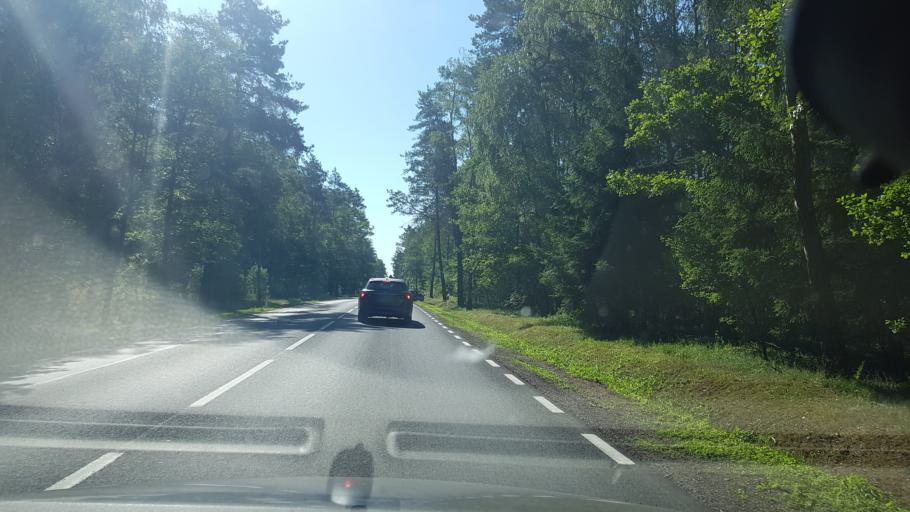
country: PL
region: Masovian Voivodeship
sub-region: Powiat wyszkowski
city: Branszczyk
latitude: 52.5677
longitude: 21.5494
